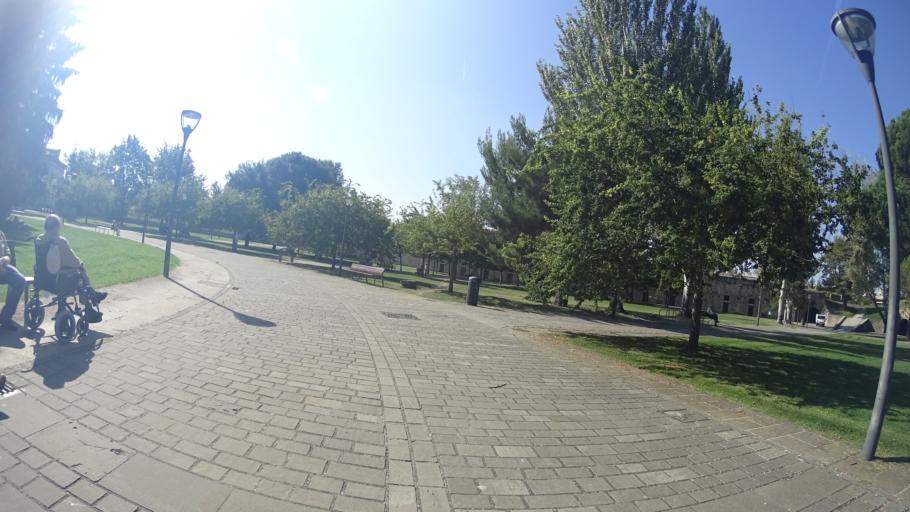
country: ES
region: Navarre
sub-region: Provincia de Navarra
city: Primer Ensanche
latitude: 42.8124
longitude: -1.6494
